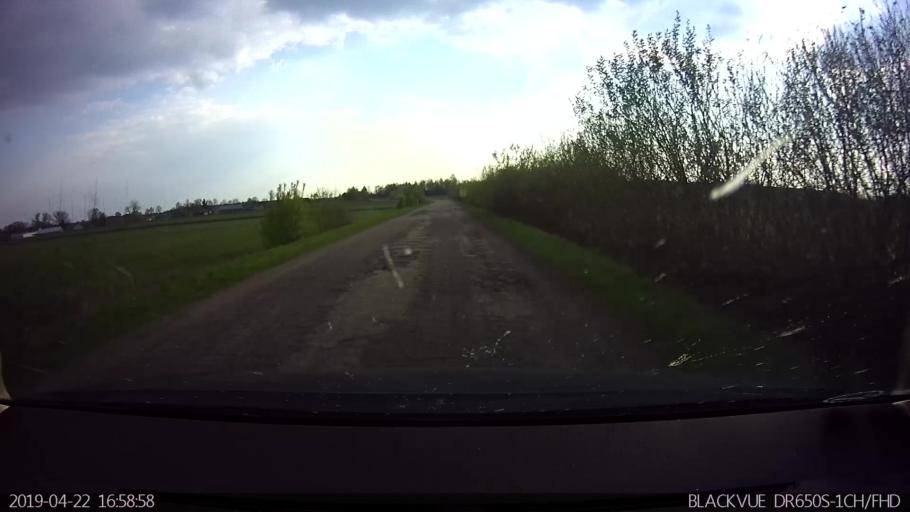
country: PL
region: Podlasie
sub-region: Powiat siemiatycki
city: Drohiczyn
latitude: 52.4661
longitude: 22.7447
